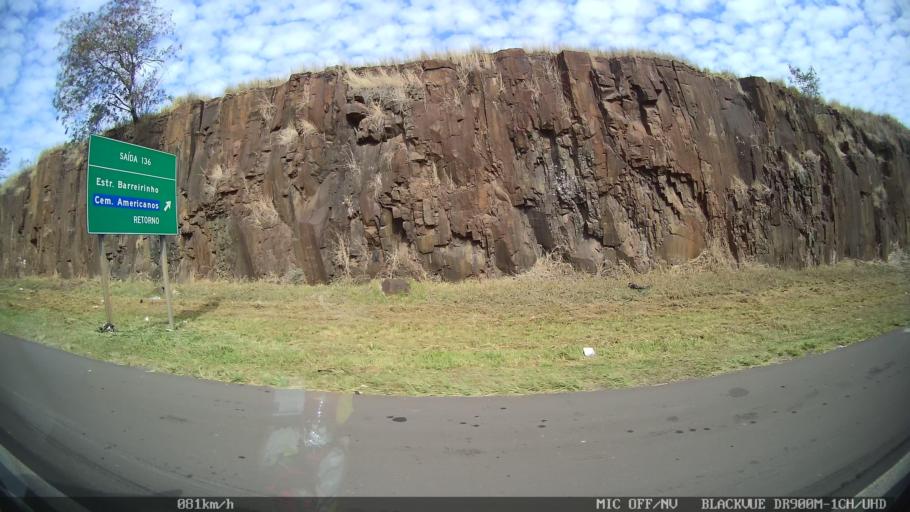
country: BR
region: Sao Paulo
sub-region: Santa Barbara D'Oeste
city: Santa Barbara d'Oeste
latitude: -22.7659
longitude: -47.4076
